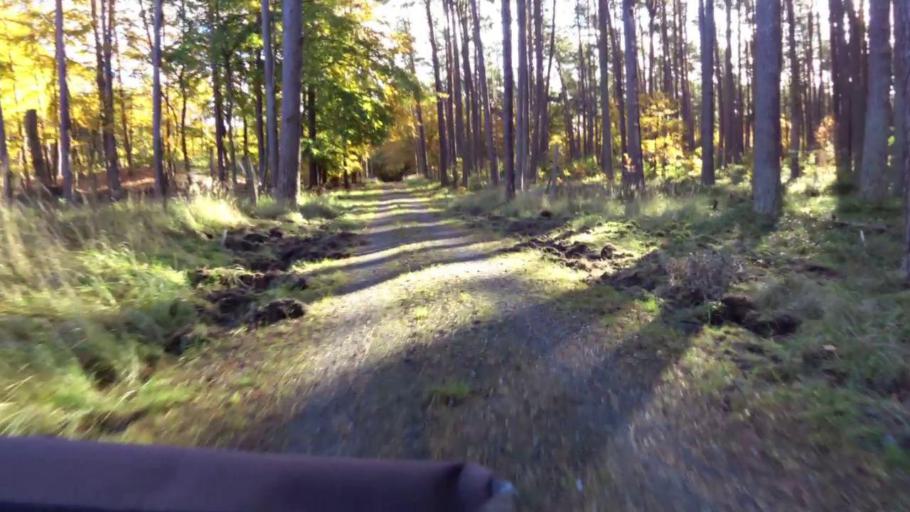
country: PL
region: West Pomeranian Voivodeship
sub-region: Powiat kamienski
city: Miedzyzdroje
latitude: 53.8668
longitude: 14.4964
